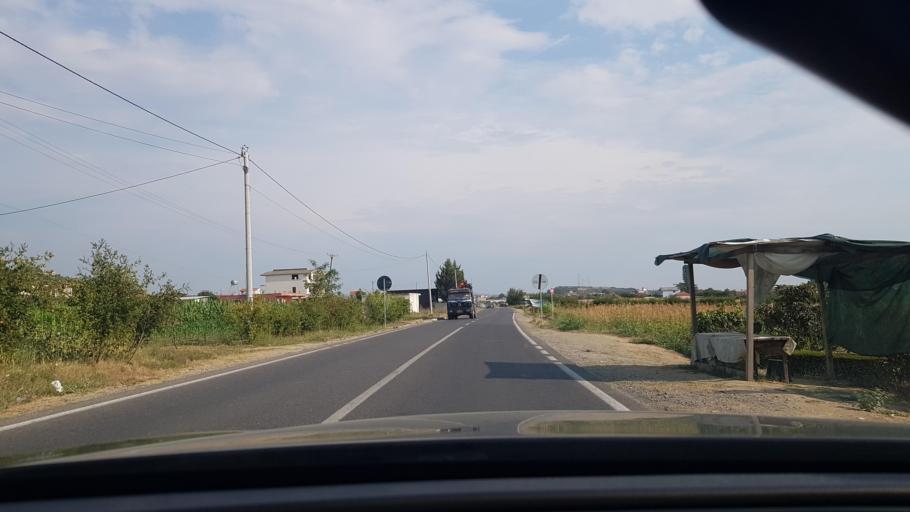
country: AL
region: Durres
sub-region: Rrethi i Durresit
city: Manze
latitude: 41.4546
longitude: 19.5681
